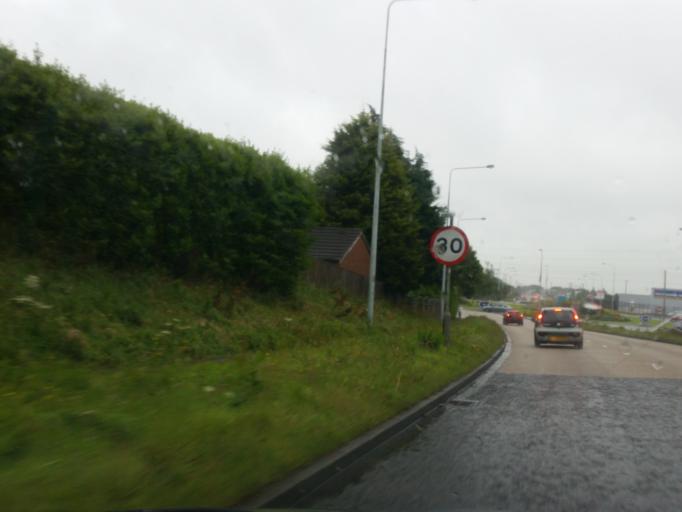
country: GB
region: Northern Ireland
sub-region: North Down District
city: Bangor
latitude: 54.6455
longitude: -5.6780
